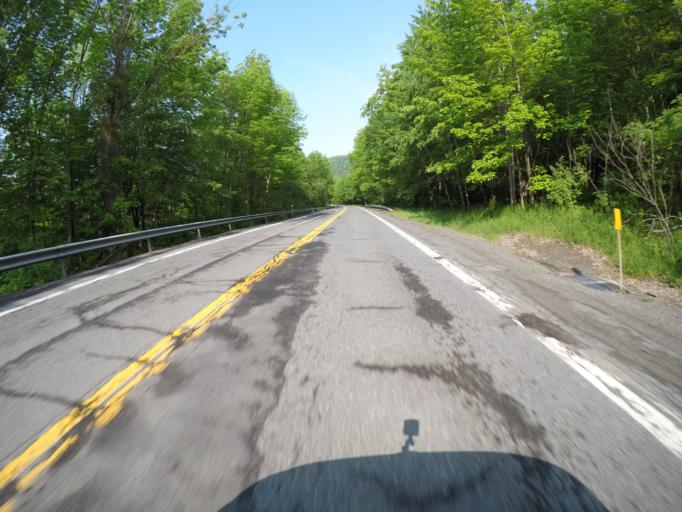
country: US
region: New York
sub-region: Sullivan County
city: Livingston Manor
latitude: 42.1035
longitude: -74.7878
